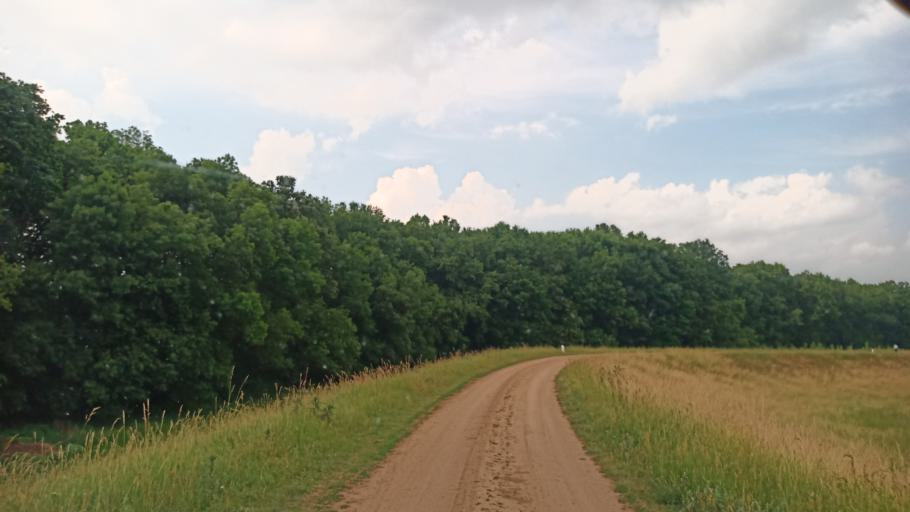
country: HU
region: Bekes
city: Doboz
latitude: 46.7040
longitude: 21.2773
